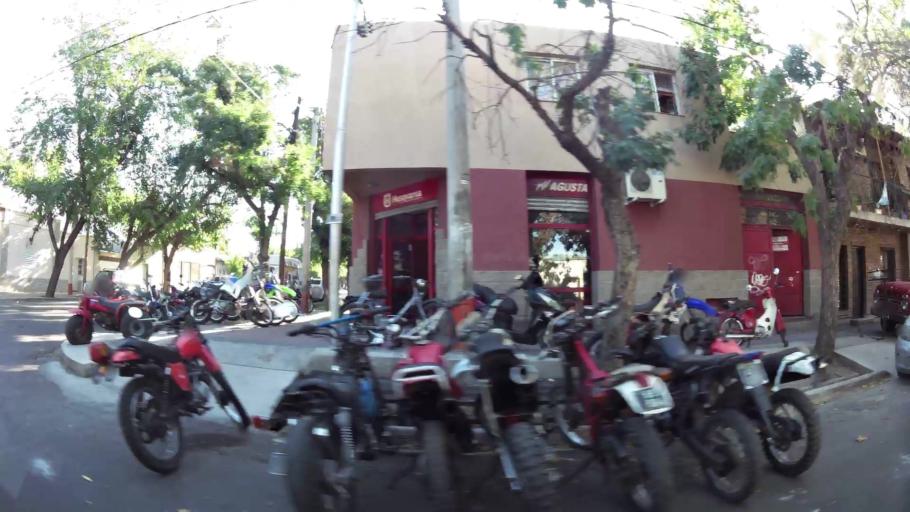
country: AR
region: Mendoza
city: Mendoza
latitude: -32.9024
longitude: -68.8352
